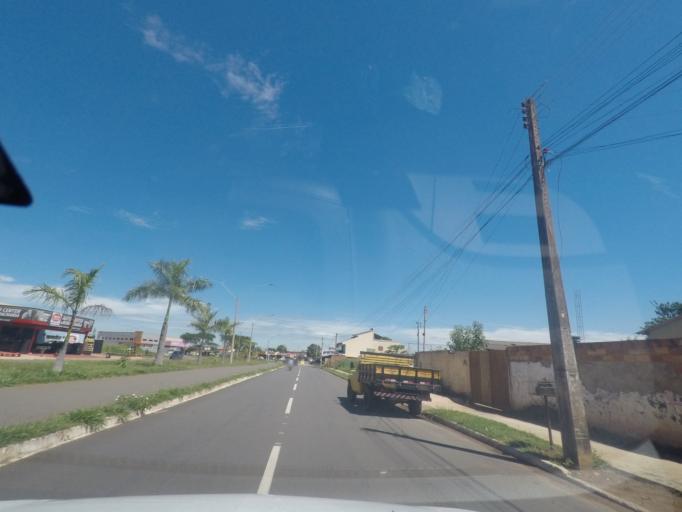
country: BR
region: Goias
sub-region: Aparecida De Goiania
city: Aparecida de Goiania
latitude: -16.7814
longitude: -49.3334
